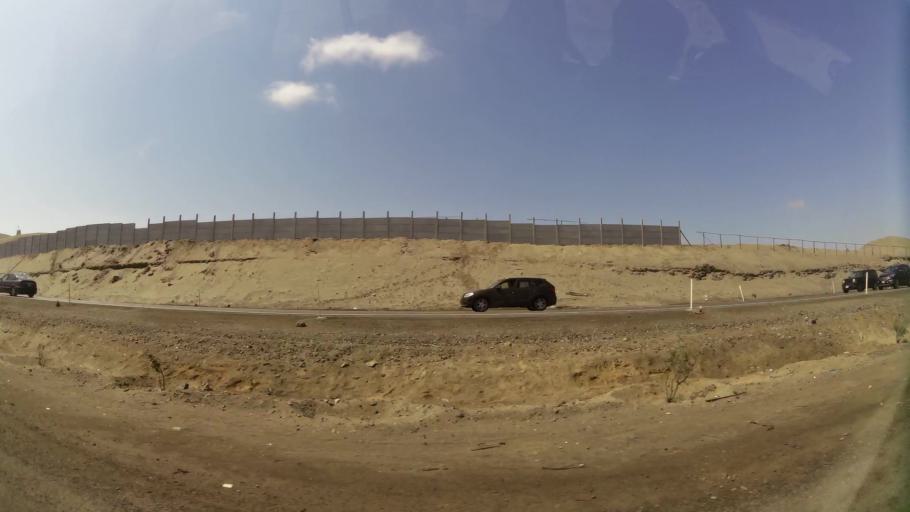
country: PE
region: Lima
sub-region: Provincia de Canete
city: Quilmana
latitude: -12.9661
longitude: -76.4990
